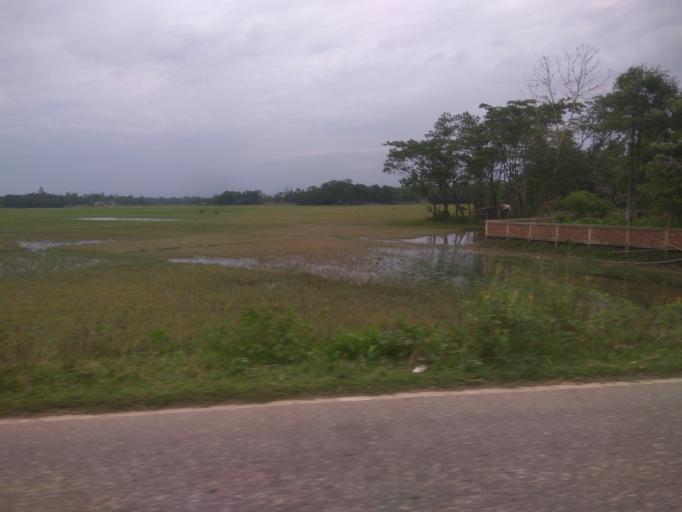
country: IN
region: Assam
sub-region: Karimganj
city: Karimganj
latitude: 24.9473
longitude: 92.2371
